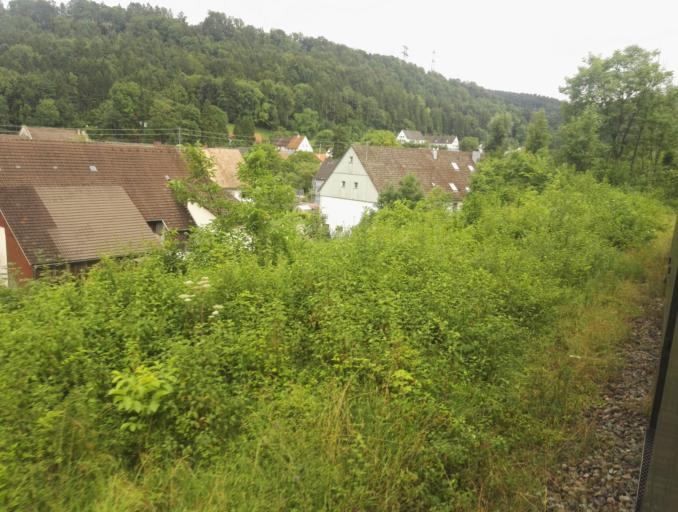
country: CH
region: Schaffhausen
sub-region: Bezirk Schleitheim
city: Schleitheim
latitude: 47.7860
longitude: 8.4950
